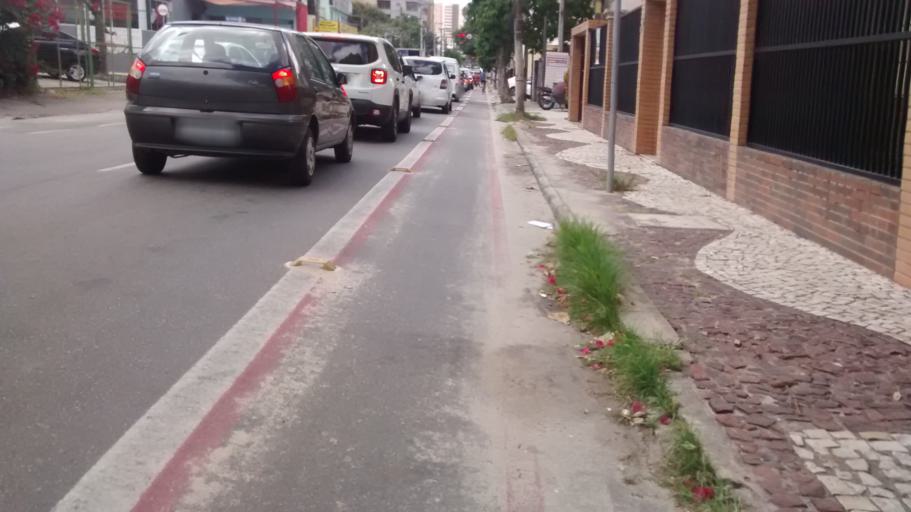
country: BR
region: Ceara
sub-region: Fortaleza
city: Fortaleza
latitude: -3.7352
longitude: -38.5115
